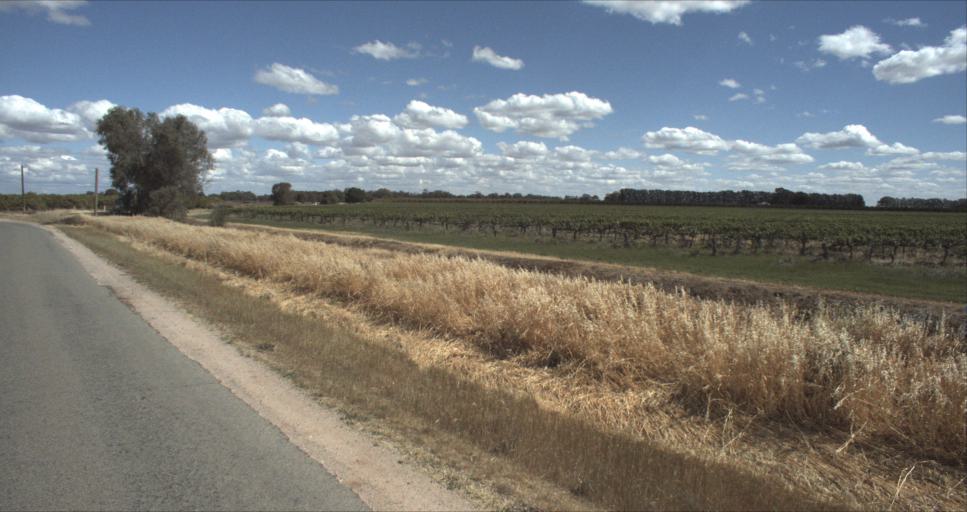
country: AU
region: New South Wales
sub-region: Leeton
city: Leeton
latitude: -34.5072
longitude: 146.2221
